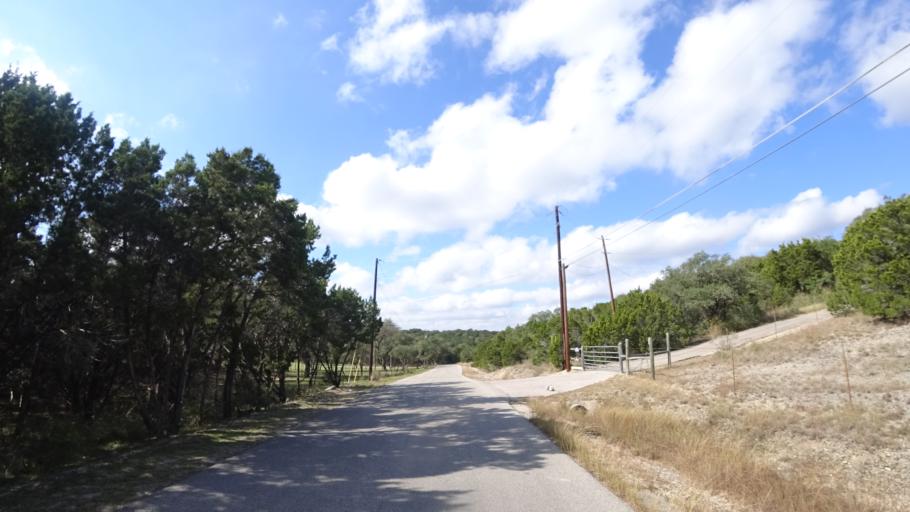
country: US
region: Texas
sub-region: Travis County
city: Bee Cave
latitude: 30.2563
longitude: -97.9376
